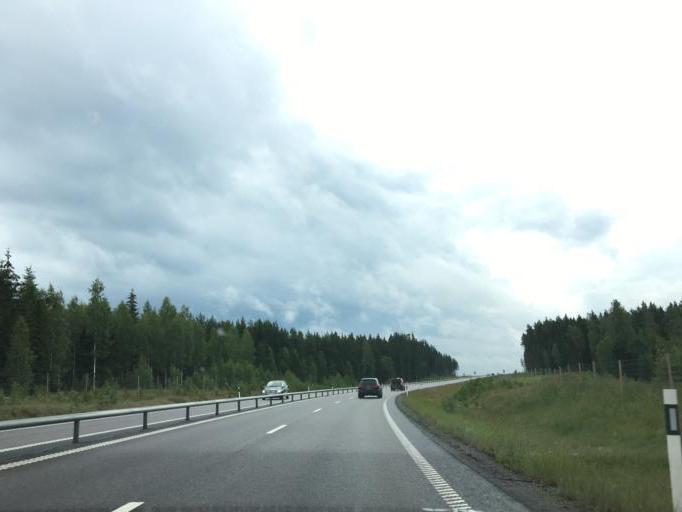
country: SE
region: Soedermanland
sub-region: Katrineholms Kommun
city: Katrineholm
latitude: 59.0056
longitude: 16.2428
